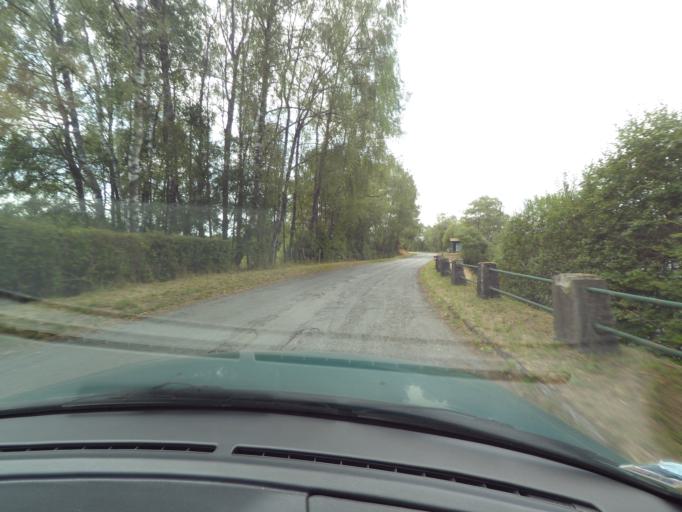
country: FR
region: Limousin
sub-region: Departement de la Correze
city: Bugeat
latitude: 45.7305
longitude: 1.9975
